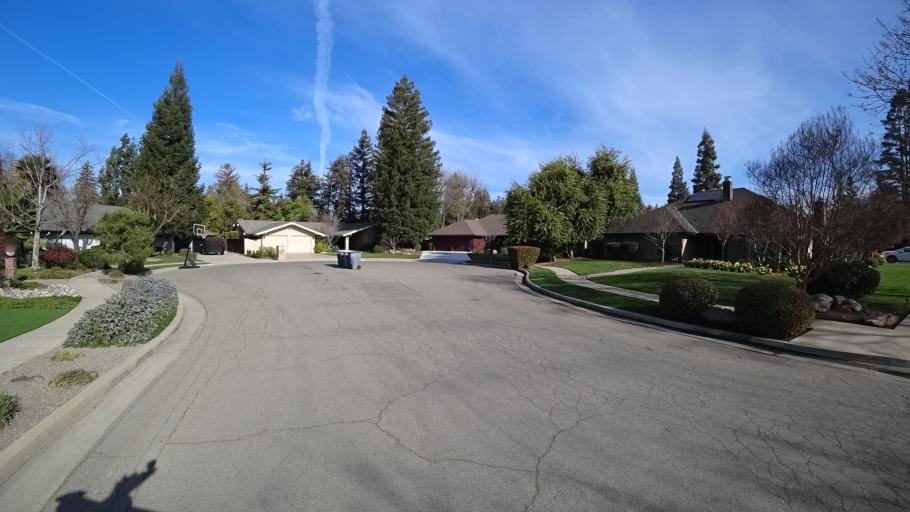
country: US
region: California
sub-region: Fresno County
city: Clovis
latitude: 36.8642
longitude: -119.7768
